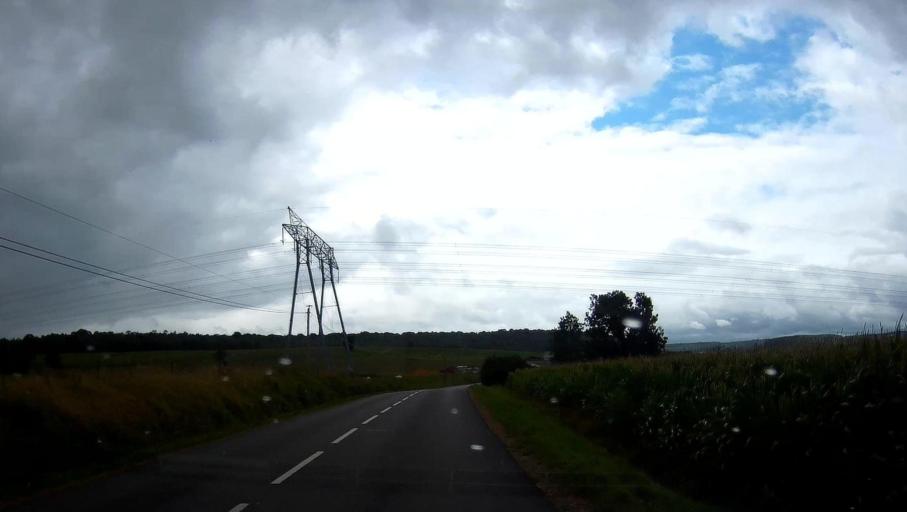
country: FR
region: Champagne-Ardenne
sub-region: Departement des Ardennes
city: Tournes
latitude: 49.7561
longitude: 4.6231
